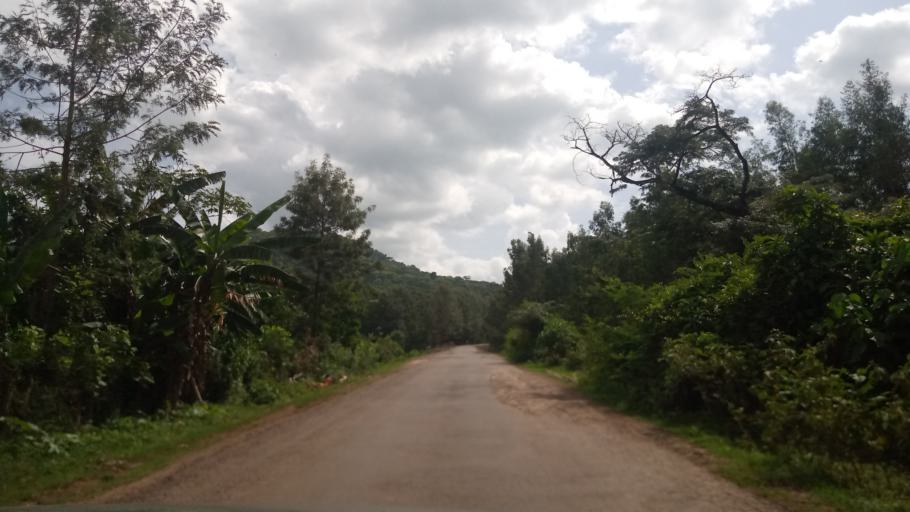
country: ET
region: Oromiya
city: Agaro
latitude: 7.9209
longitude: 36.5248
